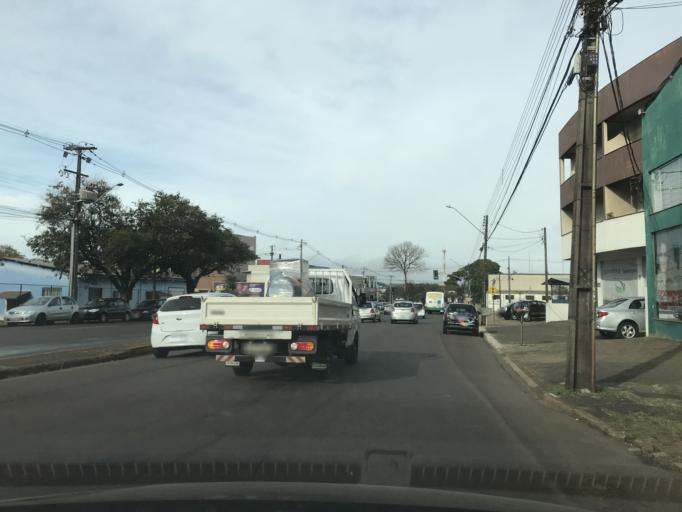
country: BR
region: Parana
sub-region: Cascavel
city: Cascavel
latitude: -24.9621
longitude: -53.4815
